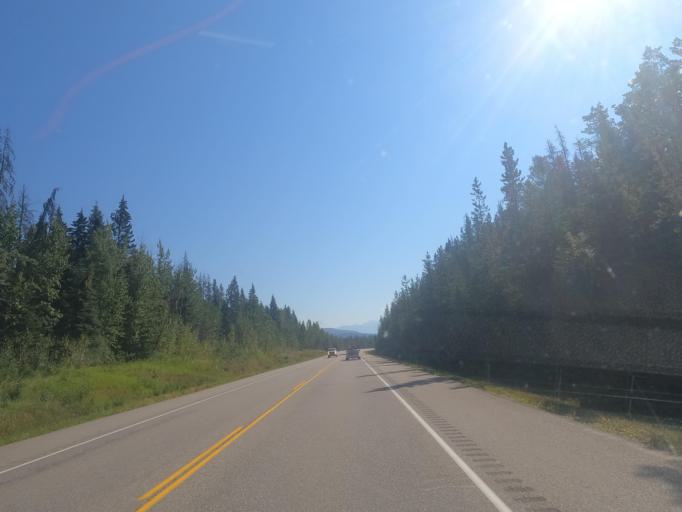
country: CA
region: Alberta
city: Jasper Park Lodge
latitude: 52.8765
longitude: -118.3215
